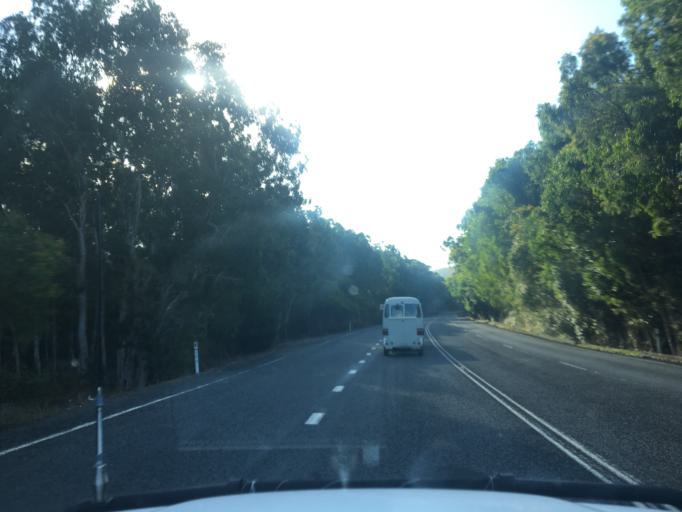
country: AU
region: Queensland
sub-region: Cairns
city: Palm Cove
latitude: -16.6770
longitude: 145.5704
